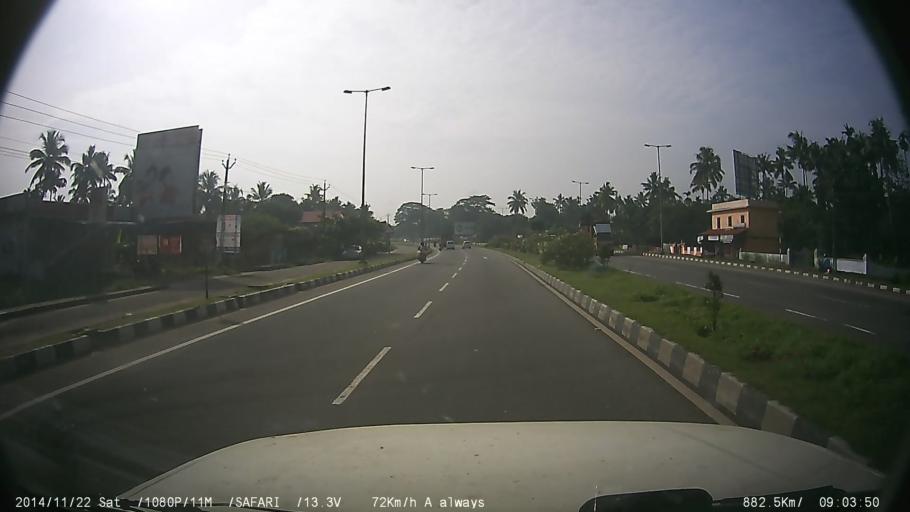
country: IN
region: Kerala
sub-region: Thrissur District
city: Kizhake Chalakudi
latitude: 10.3536
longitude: 76.3176
